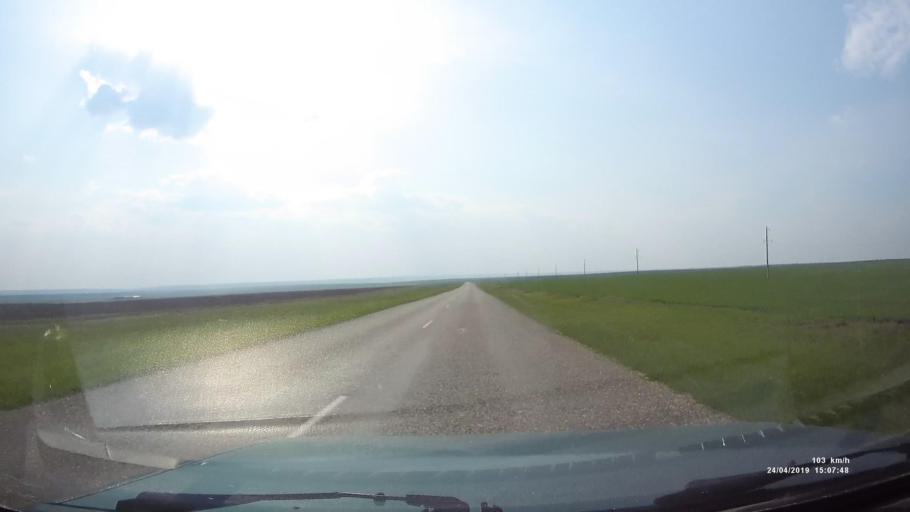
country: RU
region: Rostov
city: Remontnoye
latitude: 46.5599
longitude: 43.3971
